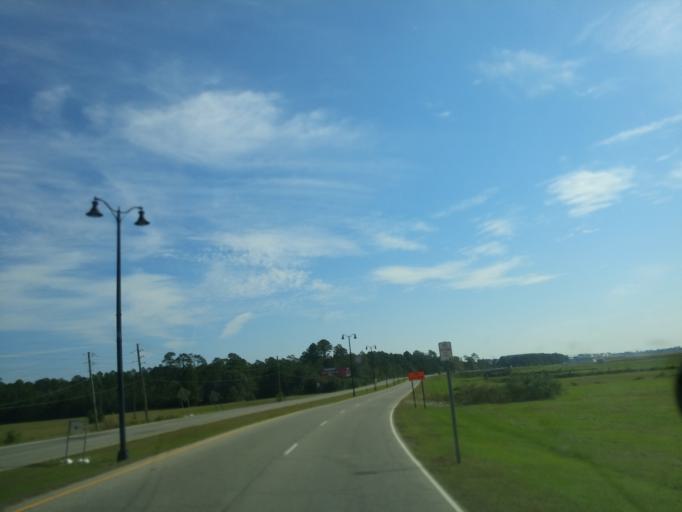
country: US
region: Mississippi
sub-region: Harrison County
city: West Gulfport
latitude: 30.4199
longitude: -89.0872
